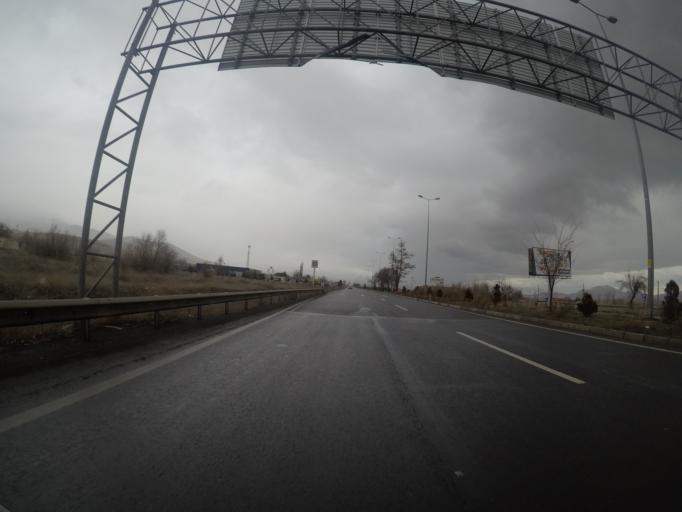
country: TR
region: Kayseri
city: Incesu
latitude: 38.6832
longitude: 35.2364
